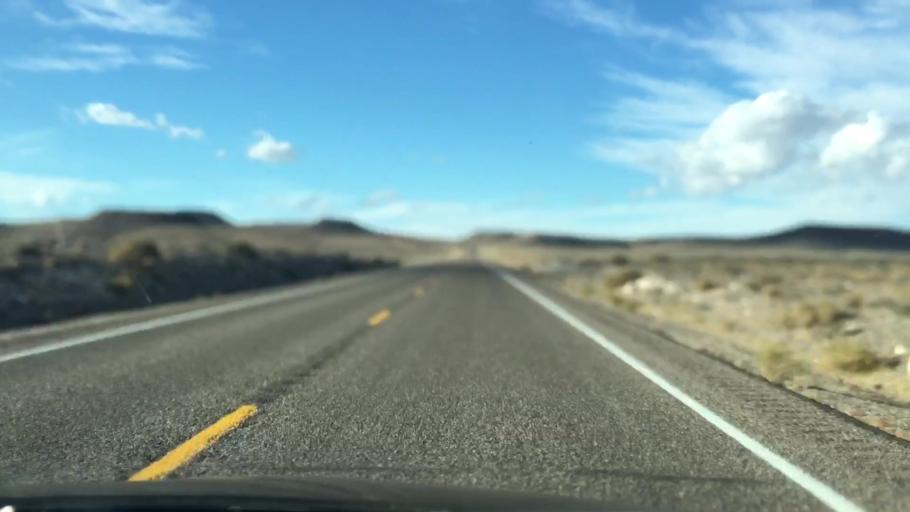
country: US
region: Nevada
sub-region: Esmeralda County
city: Goldfield
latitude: 37.3694
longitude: -117.1249
